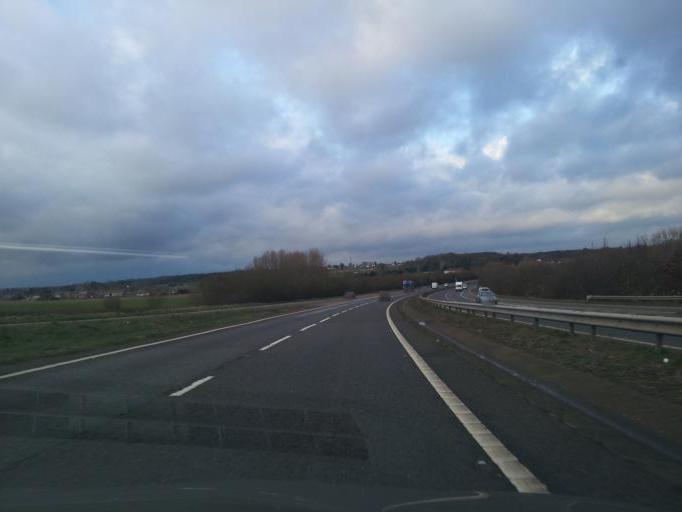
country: GB
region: England
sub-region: Norfolk
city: Bowthorpe
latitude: 52.6274
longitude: 1.1957
